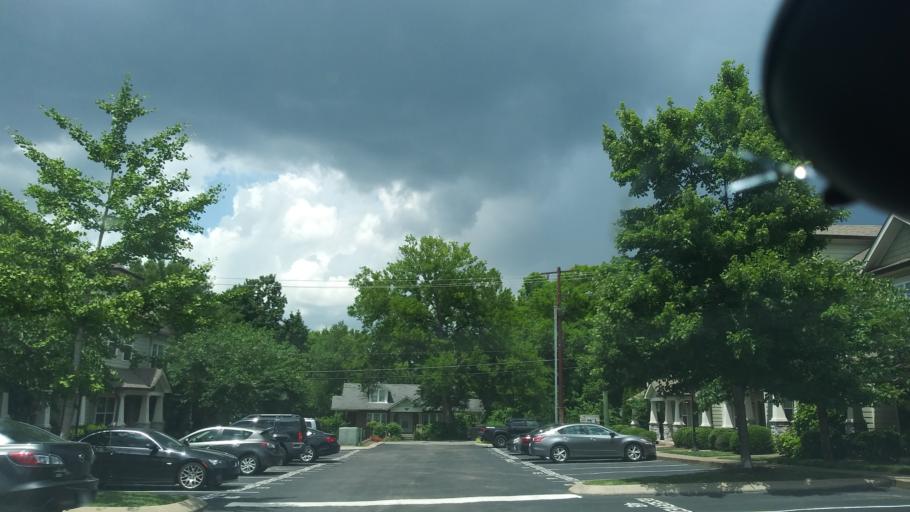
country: US
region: Tennessee
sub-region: Davidson County
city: Oak Hill
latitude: 36.1234
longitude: -86.7615
